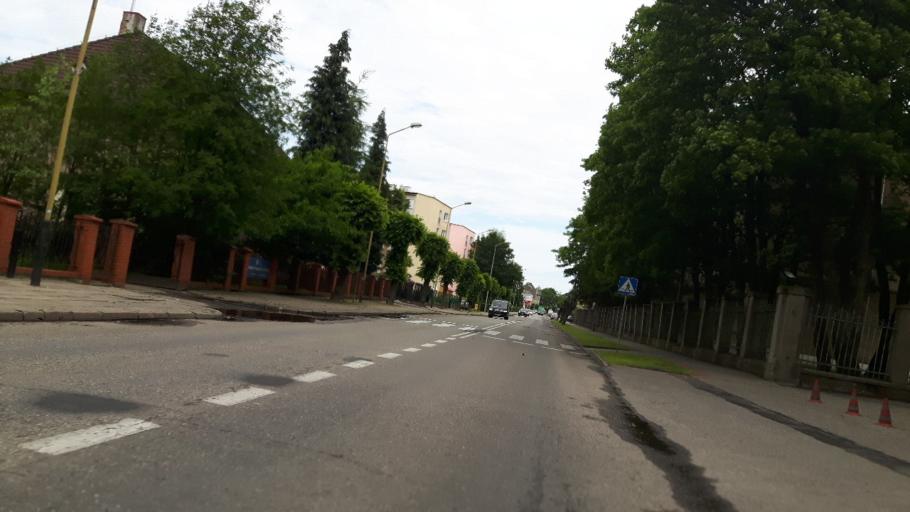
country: PL
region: West Pomeranian Voivodeship
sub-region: Powiat gryficki
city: Trzebiatow
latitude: 54.0537
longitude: 15.2575
